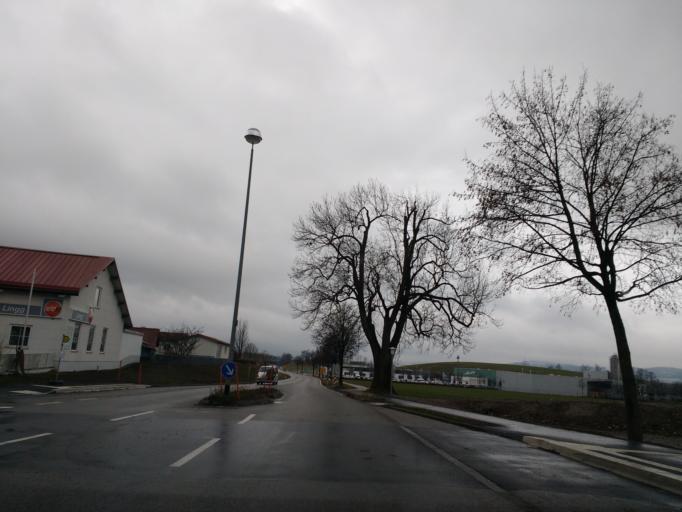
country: DE
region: Bavaria
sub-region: Swabia
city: Neuburg
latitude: 47.7631
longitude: 10.3347
